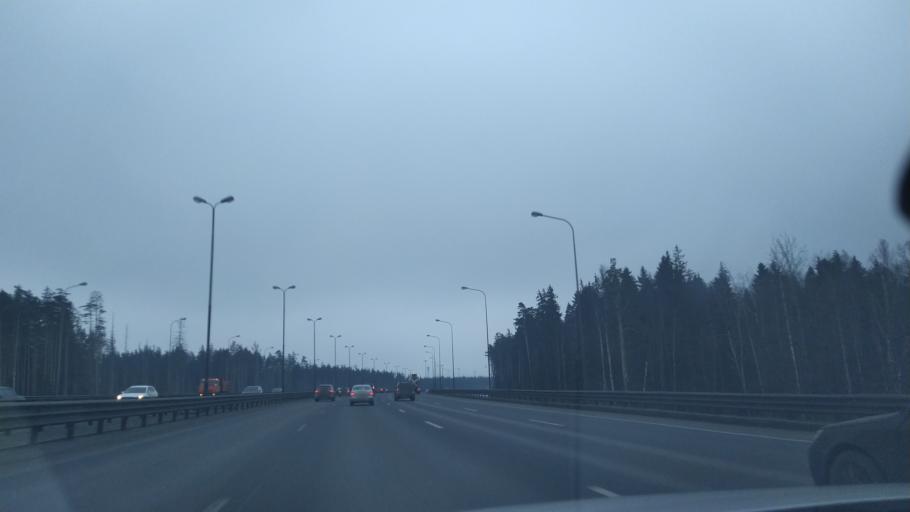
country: RU
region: Leningrad
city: Yanino Vtoroye
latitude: 59.9680
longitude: 30.5519
